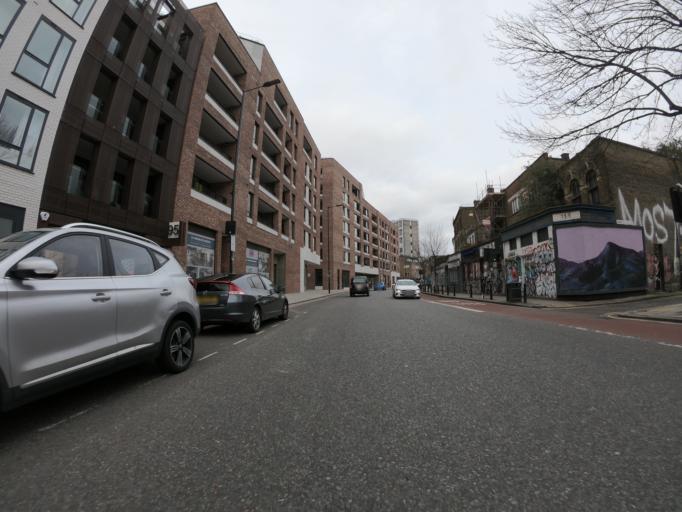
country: GB
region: England
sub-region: Greater London
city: Bethnal Green
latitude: 51.5295
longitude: -0.0748
